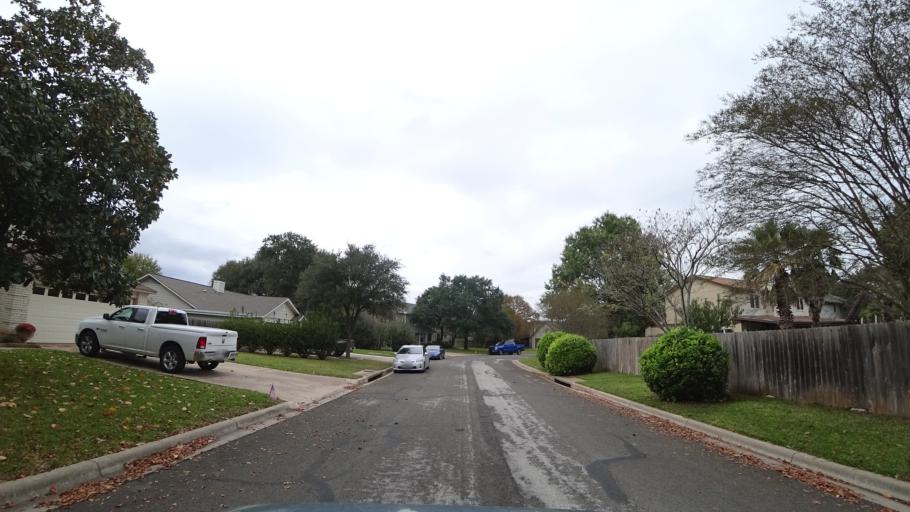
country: US
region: Texas
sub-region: Williamson County
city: Round Rock
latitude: 30.4845
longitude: -97.7048
